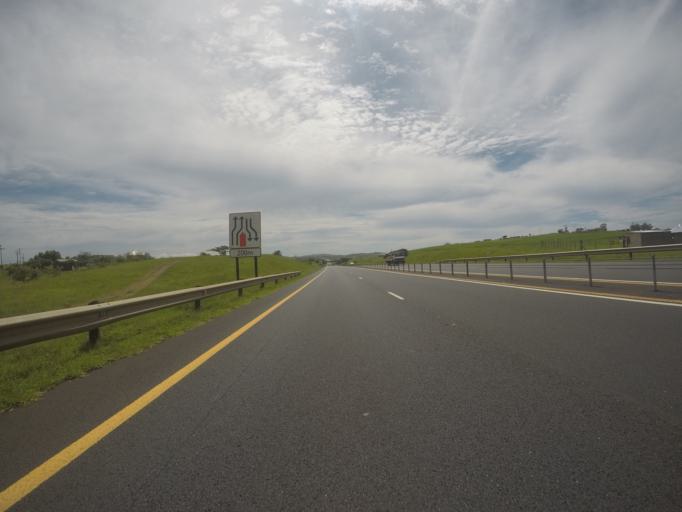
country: ZA
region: KwaZulu-Natal
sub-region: iLembe District Municipality
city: Mandeni
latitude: -29.1754
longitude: 31.5098
